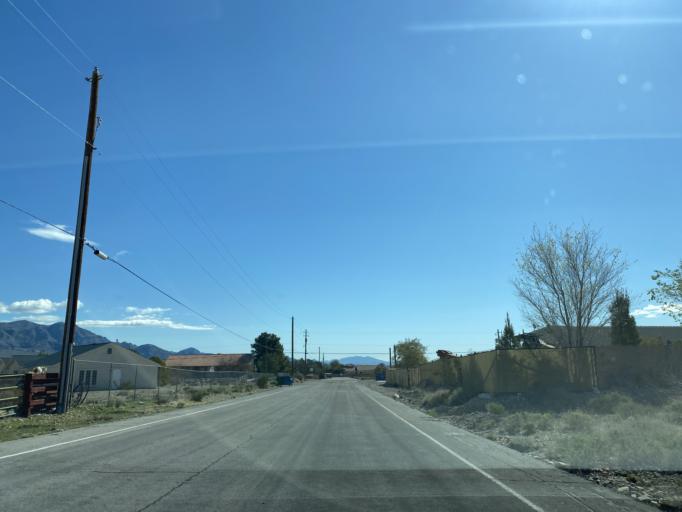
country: US
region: Nevada
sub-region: Clark County
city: North Las Vegas
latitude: 36.3302
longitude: -115.2844
